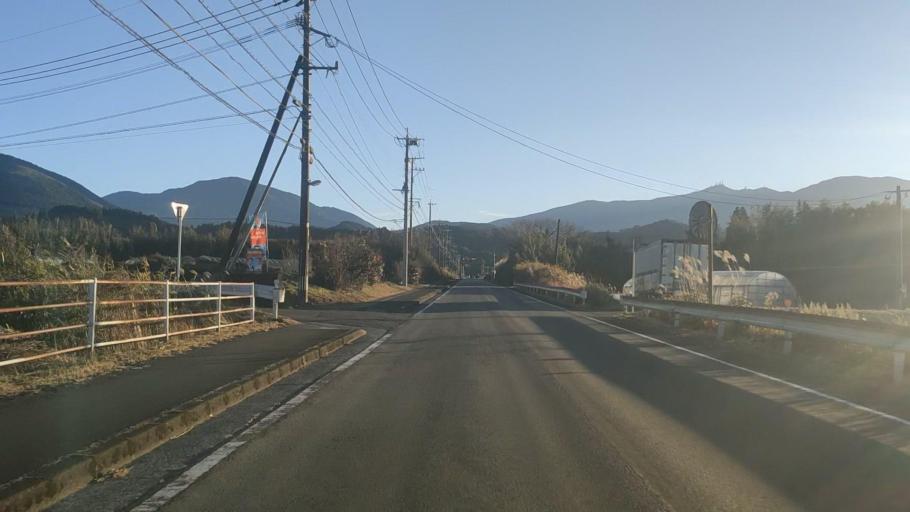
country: JP
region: Miyazaki
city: Miyazaki-shi
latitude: 31.8268
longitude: 131.2986
